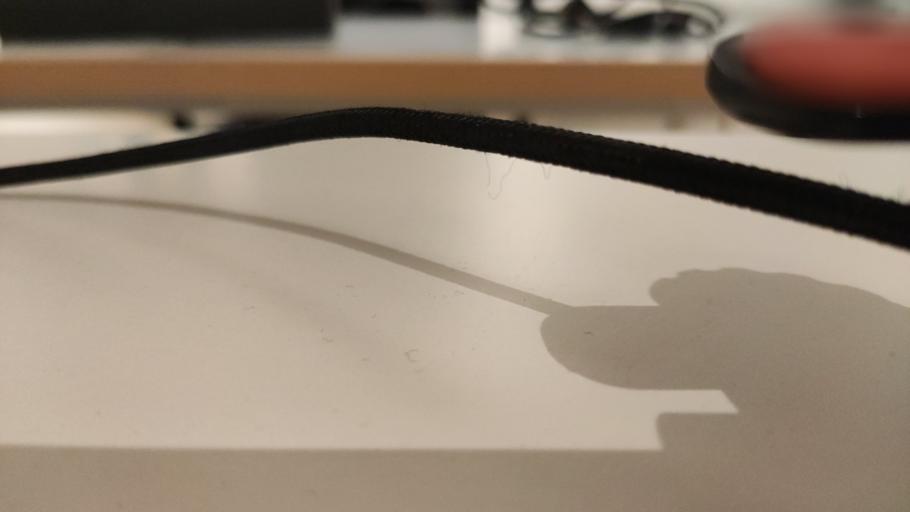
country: RU
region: Moskovskaya
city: Dorokhovo
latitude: 55.4309
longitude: 36.3526
